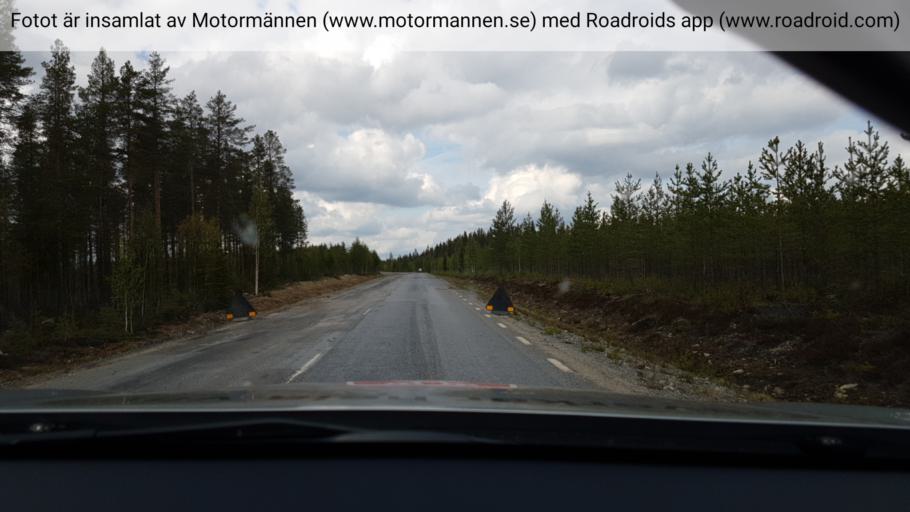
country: SE
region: Vaesterbotten
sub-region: Lycksele Kommun
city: Lycksele
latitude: 63.9714
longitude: 18.4970
